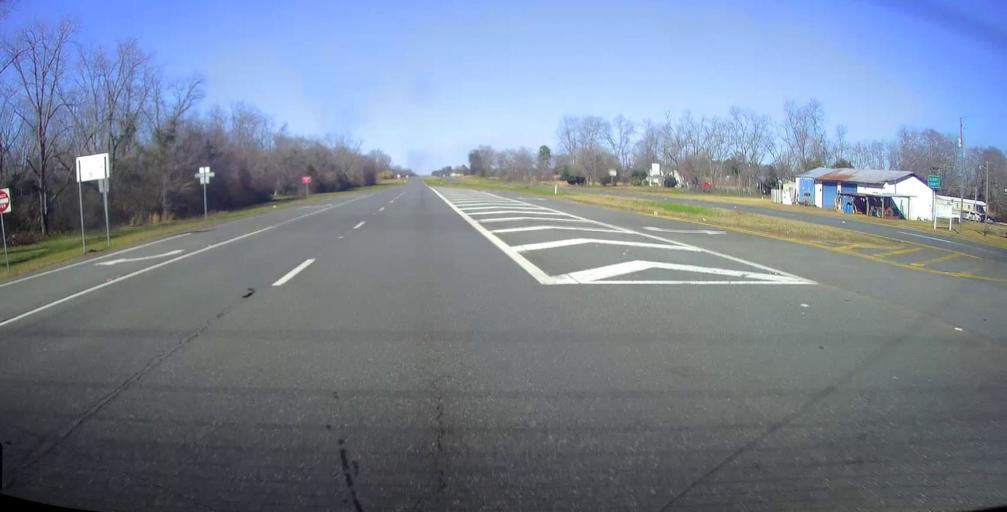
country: US
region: Georgia
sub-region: Schley County
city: Ellaville
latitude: 32.1595
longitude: -84.2703
